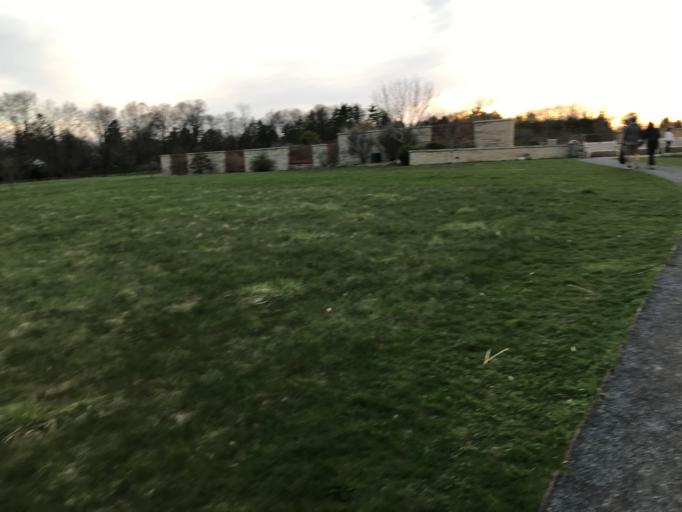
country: US
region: Pennsylvania
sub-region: Centre County
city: State College
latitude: 40.8054
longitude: -77.8672
